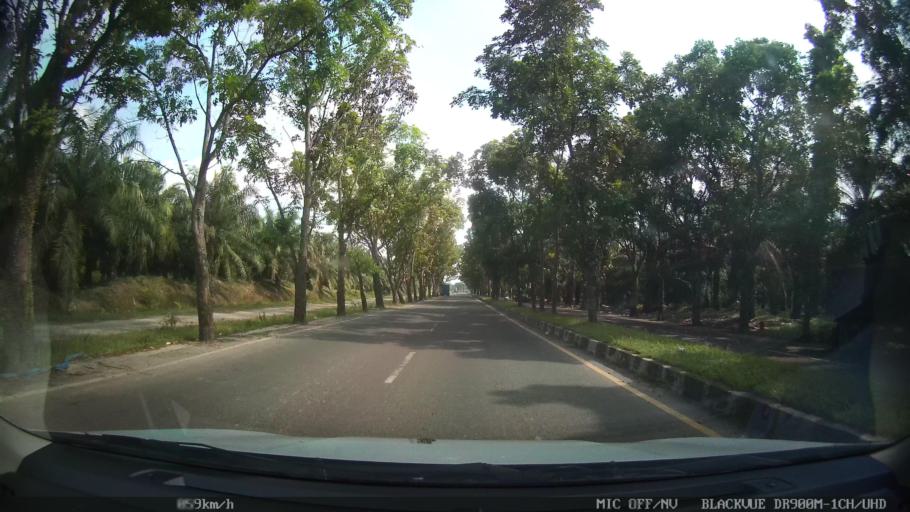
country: ID
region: North Sumatra
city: Binjai
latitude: 3.6498
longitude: 98.5356
